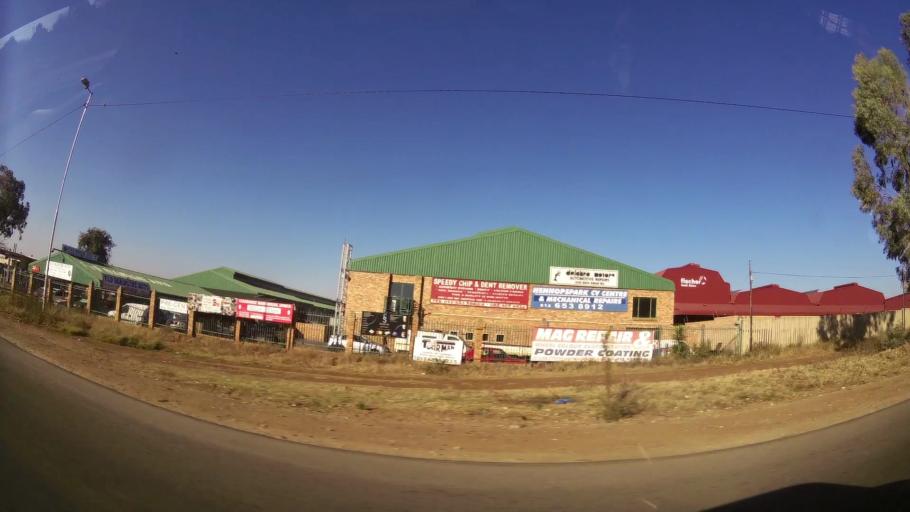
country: ZA
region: Gauteng
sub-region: City of Tshwane Metropolitan Municipality
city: Centurion
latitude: -25.8737
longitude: 28.1622
